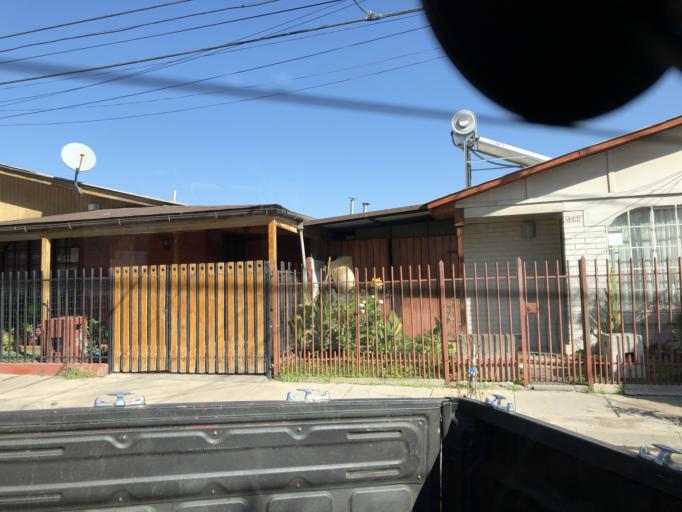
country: CL
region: Santiago Metropolitan
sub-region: Provincia de Cordillera
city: Puente Alto
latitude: -33.5751
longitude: -70.5718
